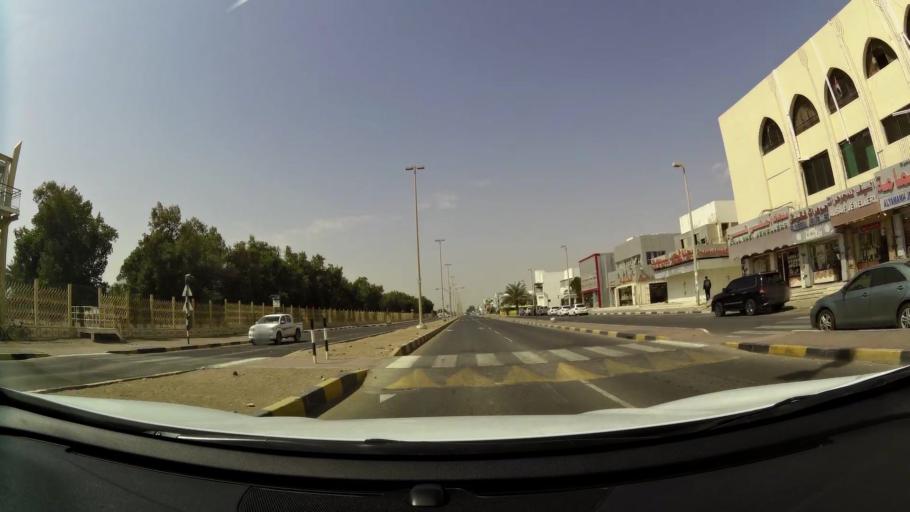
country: AE
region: Abu Dhabi
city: Abu Dhabi
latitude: 24.2846
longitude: 54.6443
